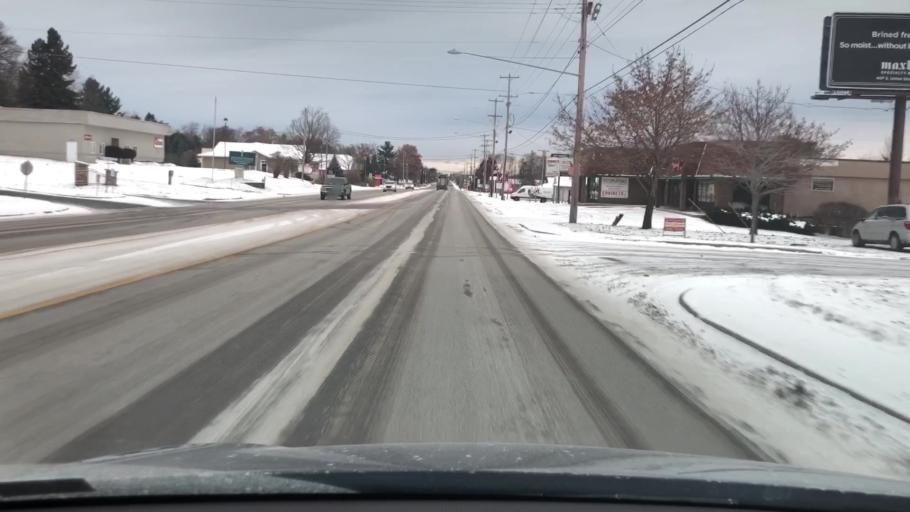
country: US
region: Michigan
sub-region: Grand Traverse County
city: Traverse City
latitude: 44.7267
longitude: -85.5953
